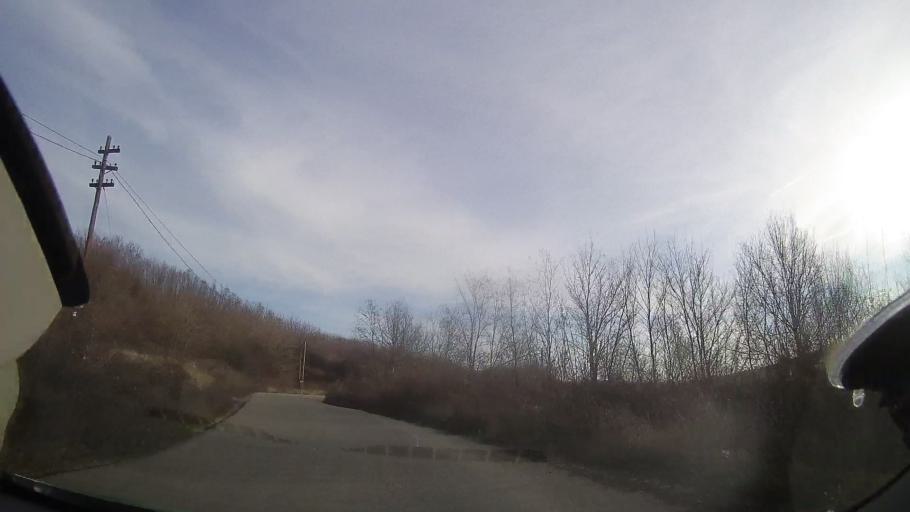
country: RO
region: Bihor
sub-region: Comuna Sarbi
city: Sarbi
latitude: 47.1871
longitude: 22.1274
